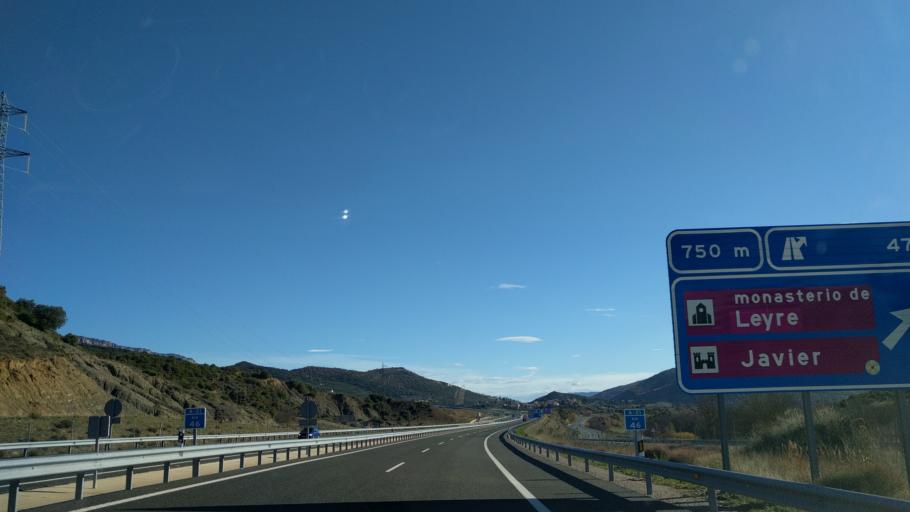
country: ES
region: Navarre
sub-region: Provincia de Navarra
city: Yesa
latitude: 42.6238
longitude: -1.2258
